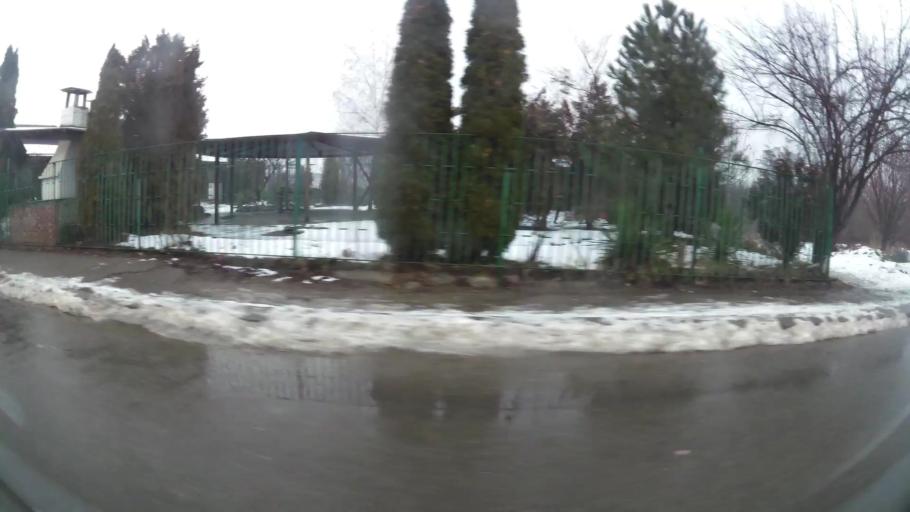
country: BG
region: Sofia-Capital
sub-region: Stolichna Obshtina
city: Sofia
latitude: 42.6849
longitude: 23.2489
